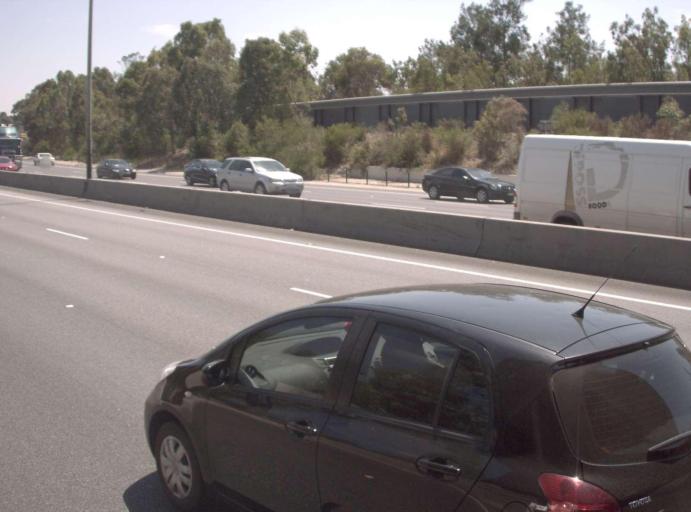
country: AU
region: Victoria
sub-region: Stonnington
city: Glen Iris
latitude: -37.8673
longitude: 145.0618
